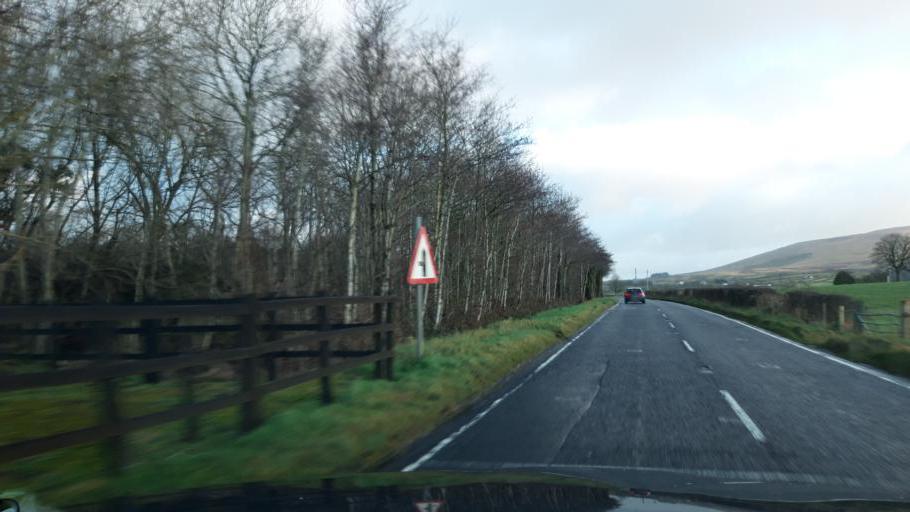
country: GB
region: Northern Ireland
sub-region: Moyle District
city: Ballycastle
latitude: 55.1409
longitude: -6.3218
